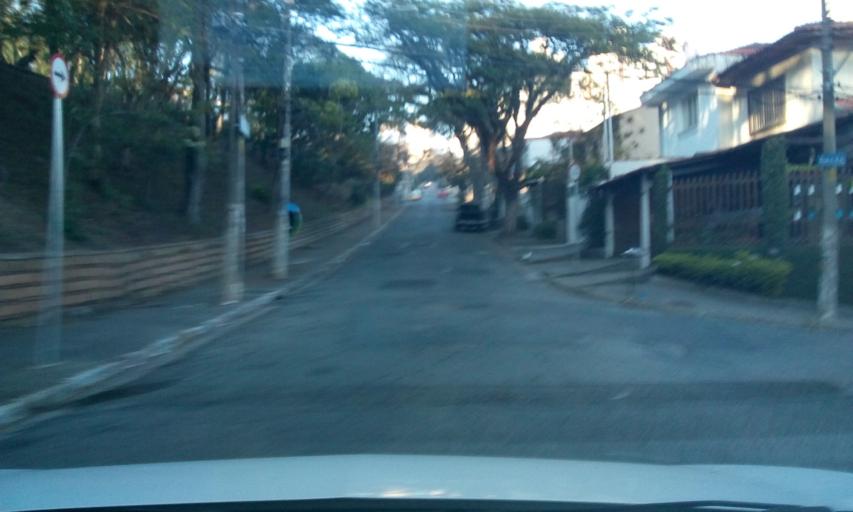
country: BR
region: Sao Paulo
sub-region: Sao Paulo
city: Sao Paulo
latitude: -23.5395
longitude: -46.6927
